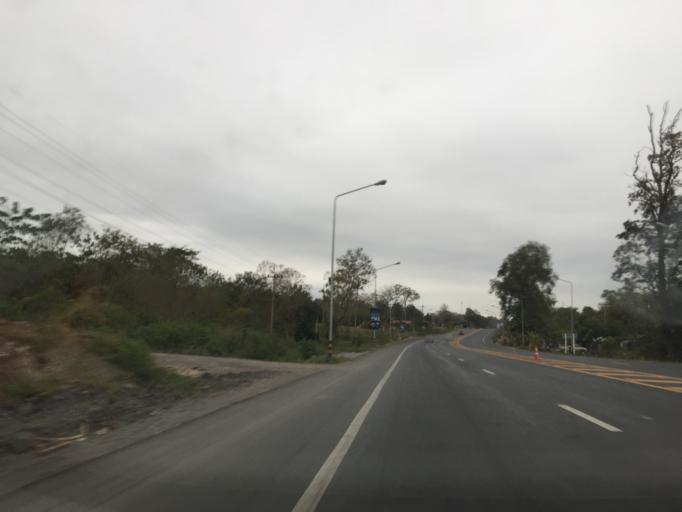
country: TH
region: Loei
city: Erawan
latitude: 17.3143
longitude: 101.9323
